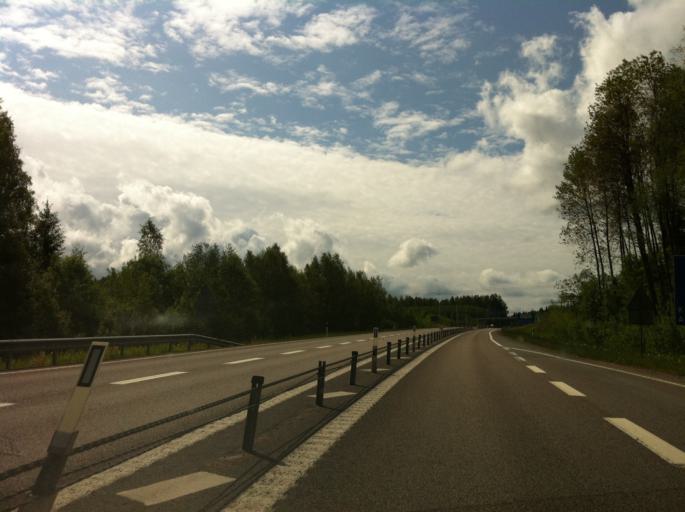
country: SE
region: Vaermland
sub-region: Karlstads Kommun
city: Edsvalla
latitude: 59.5239
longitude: 13.2151
